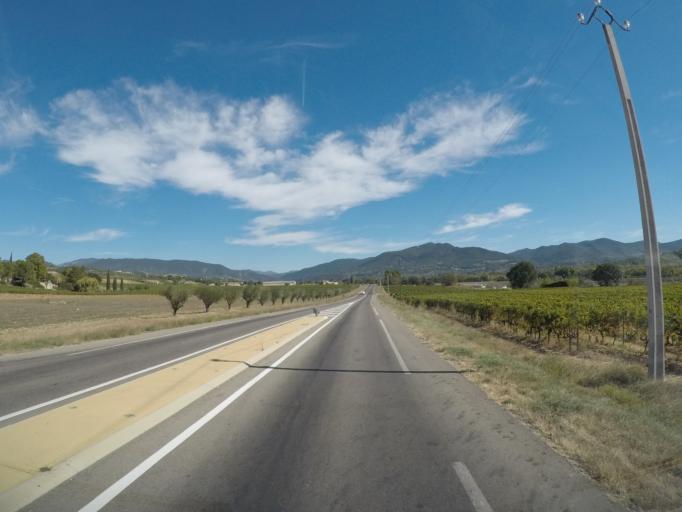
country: FR
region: Rhone-Alpes
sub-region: Departement de la Drome
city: Vinsobres
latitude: 44.3197
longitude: 5.0631
